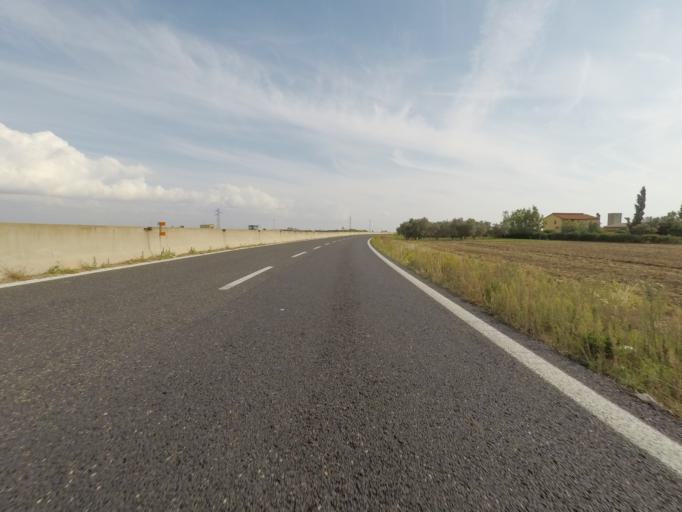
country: IT
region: Latium
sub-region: Provincia di Viterbo
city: Montalto di Castro
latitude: 42.3629
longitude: 11.5821
